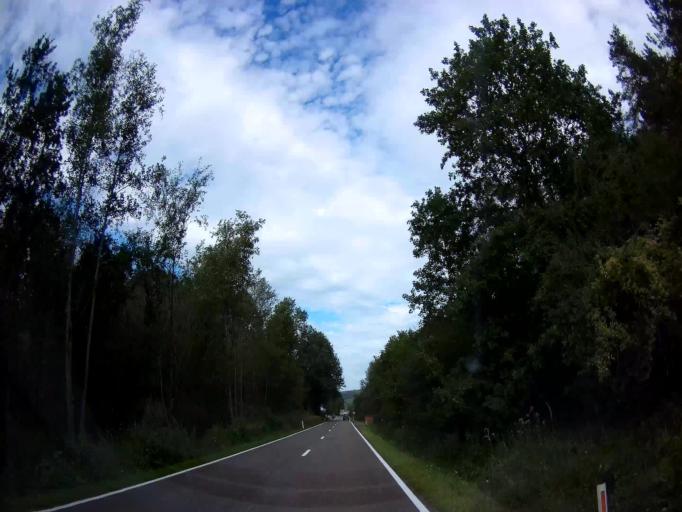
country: BE
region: Wallonia
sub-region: Province du Luxembourg
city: Durbuy
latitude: 50.3362
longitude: 5.4835
